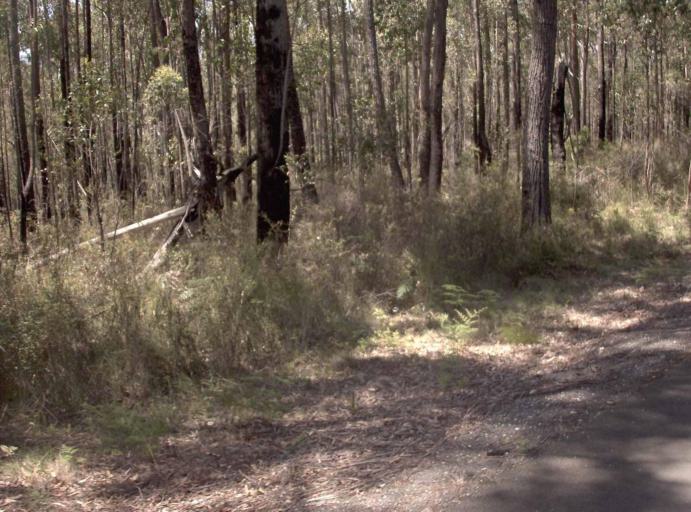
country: AU
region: New South Wales
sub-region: Bombala
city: Bombala
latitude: -37.5658
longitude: 149.0391
